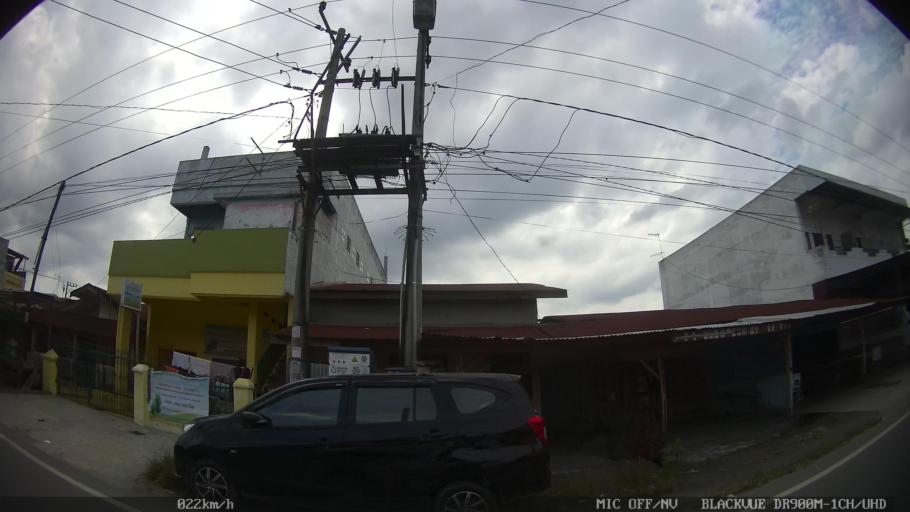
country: ID
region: North Sumatra
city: Sunggal
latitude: 3.6148
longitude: 98.6239
